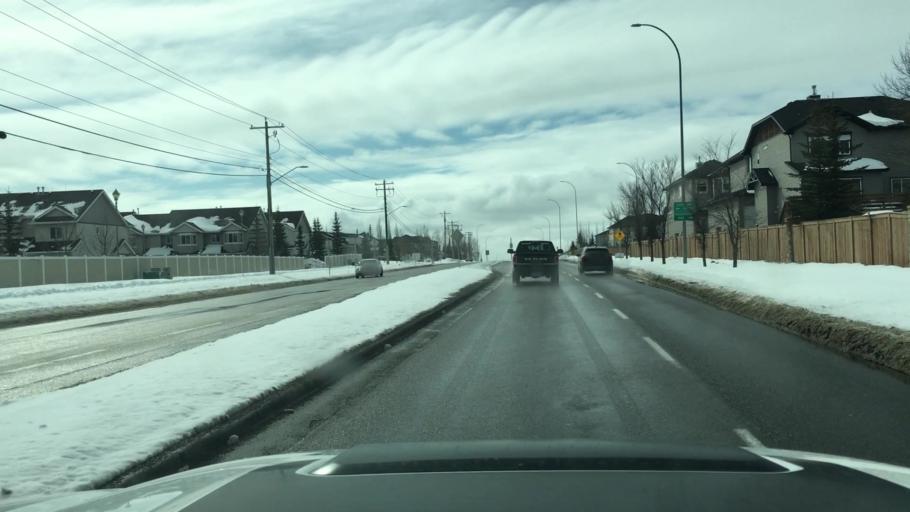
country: CA
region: Alberta
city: Calgary
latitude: 51.1536
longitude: -114.2343
